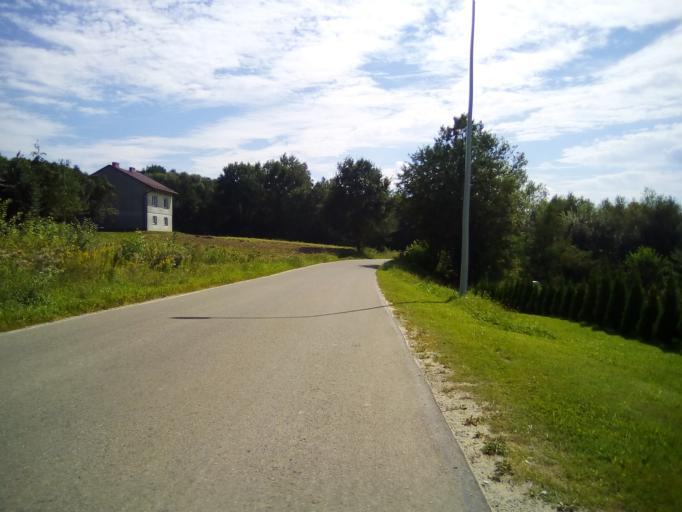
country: PL
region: Subcarpathian Voivodeship
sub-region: Powiat strzyzowski
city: Konieczkowa
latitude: 49.8210
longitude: 21.9265
